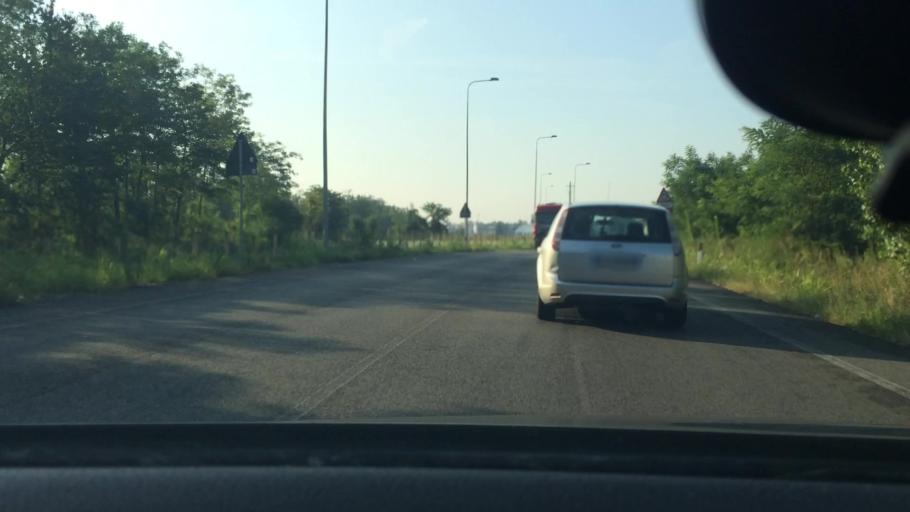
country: IT
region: Lombardy
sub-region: Citta metropolitana di Milano
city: Pregnana Milanese
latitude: 45.5243
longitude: 9.0128
